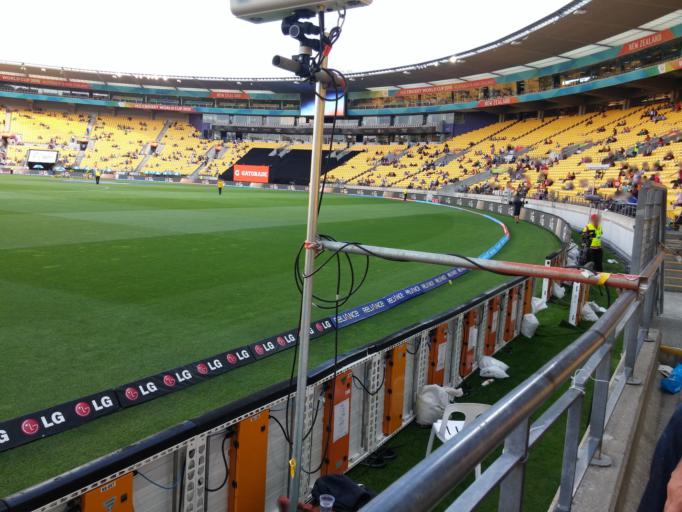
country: NZ
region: Wellington
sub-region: Wellington City
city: Wellington
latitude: -41.2729
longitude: 174.7851
